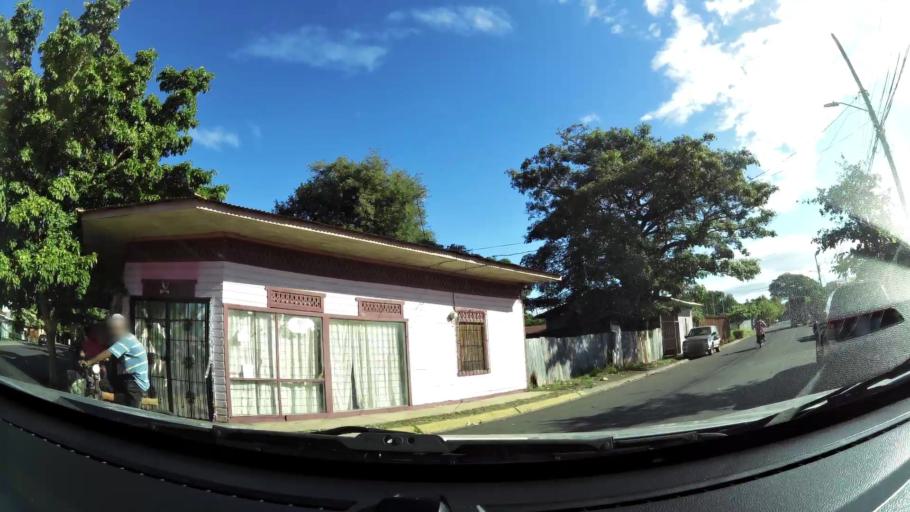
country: CR
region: Guanacaste
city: Belen
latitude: 10.4463
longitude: -85.5512
